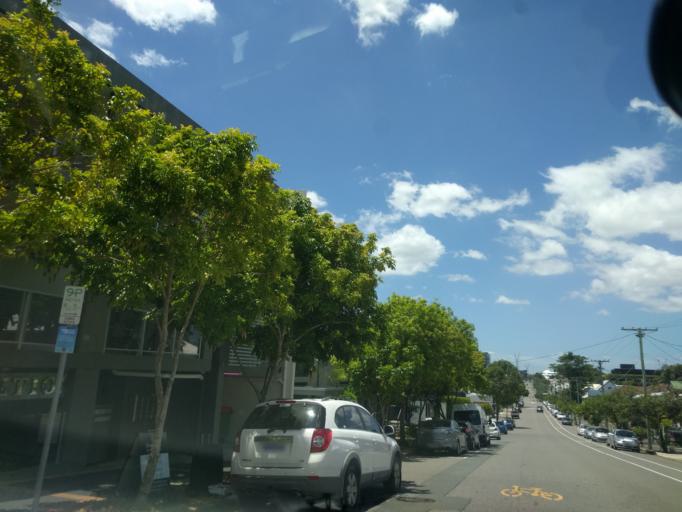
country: AU
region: Queensland
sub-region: Brisbane
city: Fortitude Valley
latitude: -27.4597
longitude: 153.0391
